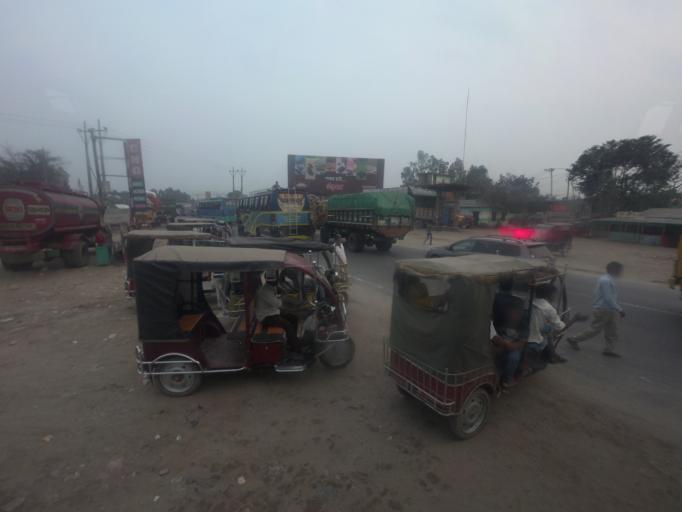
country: BD
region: Dhaka
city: Tangail
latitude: 24.2833
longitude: 89.9180
